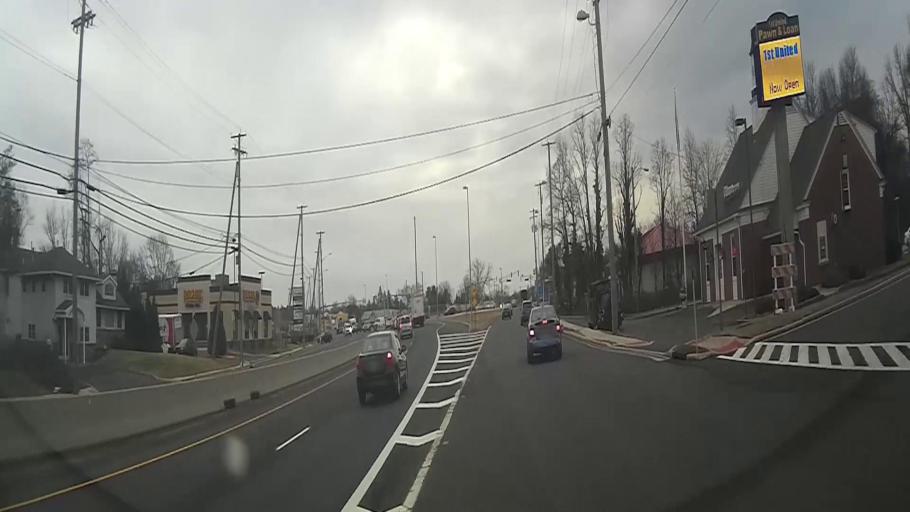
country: US
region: New Jersey
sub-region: Camden County
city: Berlin
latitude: 39.8033
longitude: -74.9319
